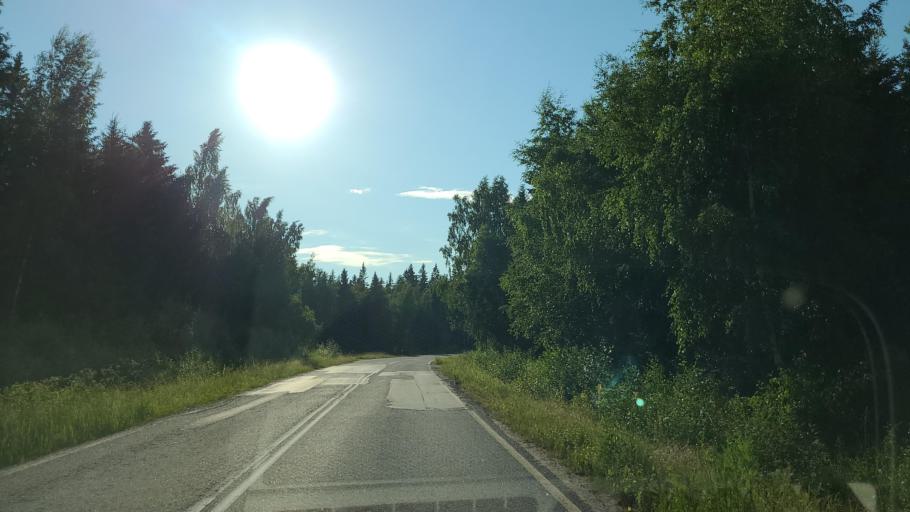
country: FI
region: Ostrobothnia
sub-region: Vaasa
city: Replot
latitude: 63.3215
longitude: 21.3492
